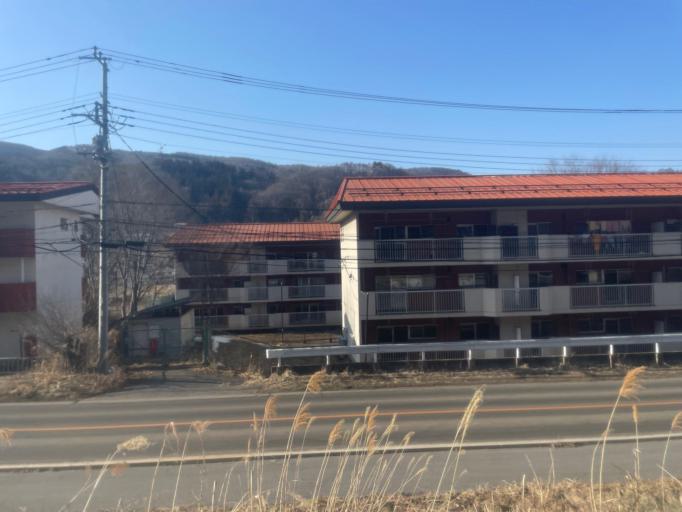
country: JP
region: Nagano
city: Komoro
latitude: 36.5361
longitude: 138.5560
